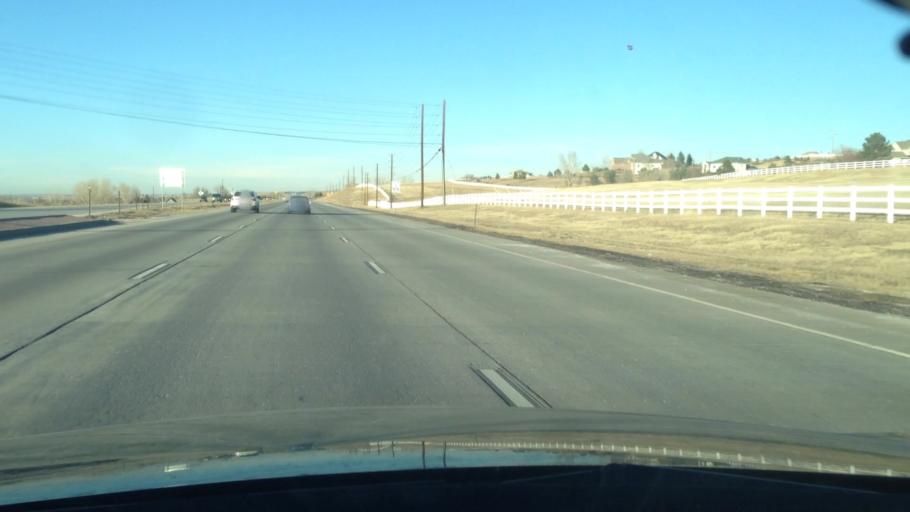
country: US
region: Colorado
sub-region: Douglas County
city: The Pinery
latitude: 39.4416
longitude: -104.7598
